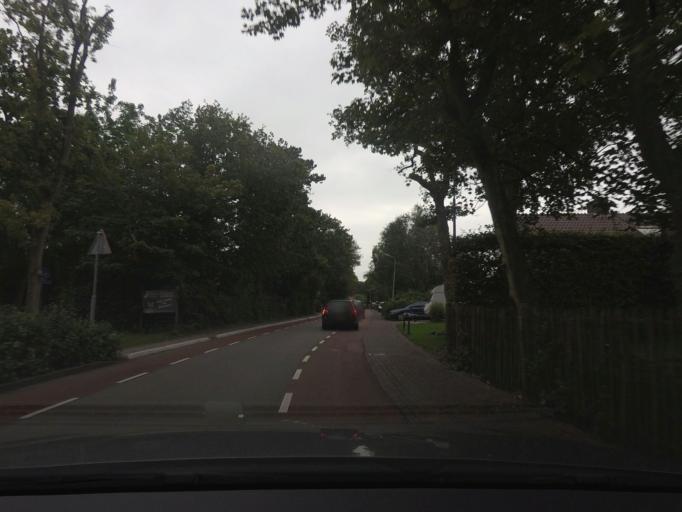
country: NL
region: North Holland
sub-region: Gemeente Schagen
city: Harenkarspel
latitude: 52.7036
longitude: 4.7016
